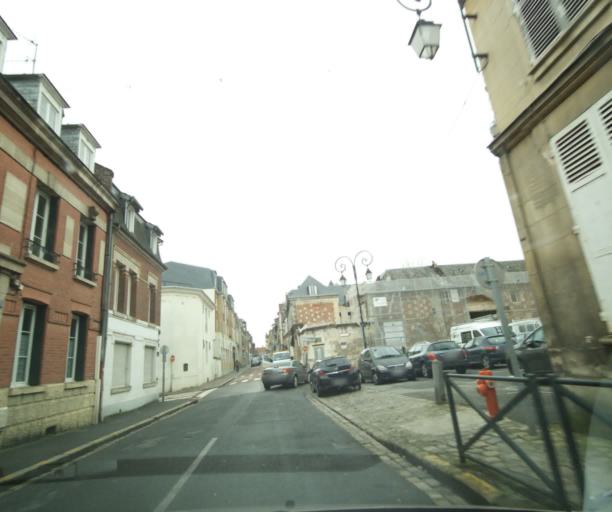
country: FR
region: Picardie
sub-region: Departement de l'Oise
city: Noyon
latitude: 49.5799
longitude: 3.0032
